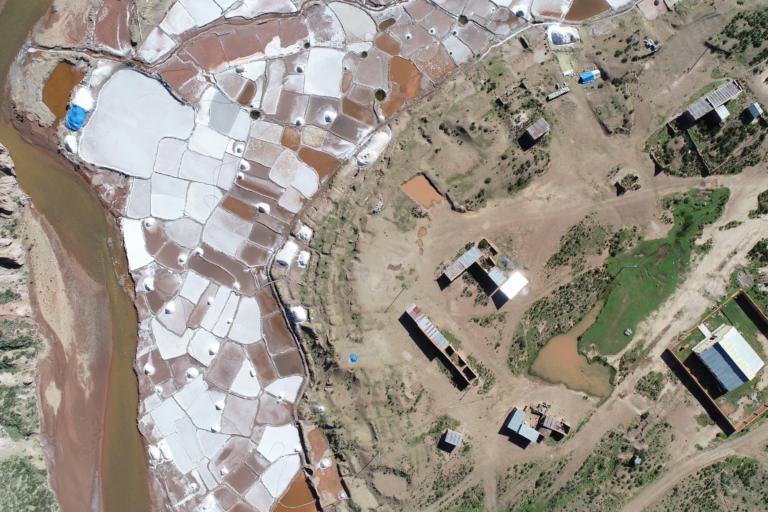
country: BO
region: La Paz
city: Curahuara de Carangas
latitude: -17.3011
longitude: -68.4862
